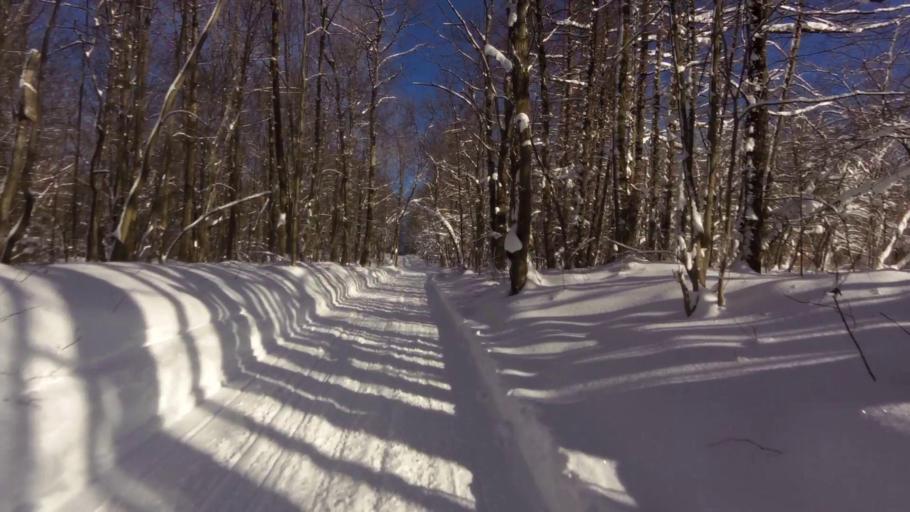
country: US
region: New York
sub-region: Chautauqua County
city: Falconer
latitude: 42.2647
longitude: -79.1417
